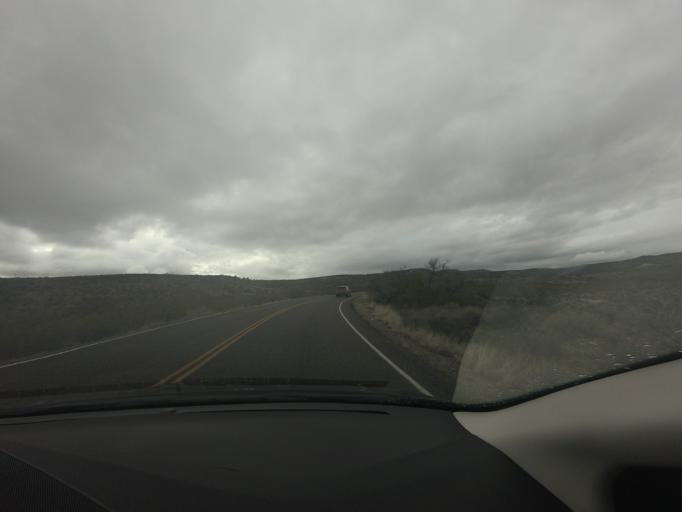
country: US
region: Arizona
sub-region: Yavapai County
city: Camp Verde
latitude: 34.6143
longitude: -111.8374
